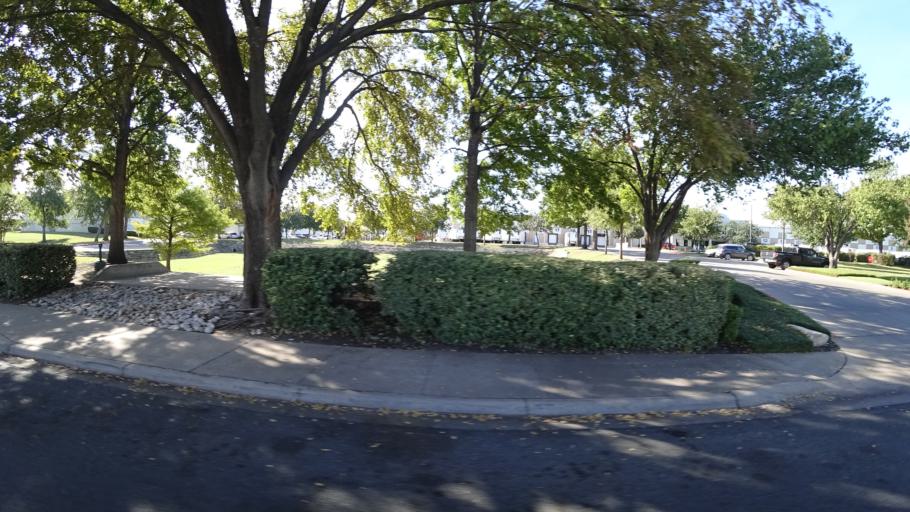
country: US
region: Texas
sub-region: Travis County
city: Austin
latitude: 30.2524
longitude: -97.6848
